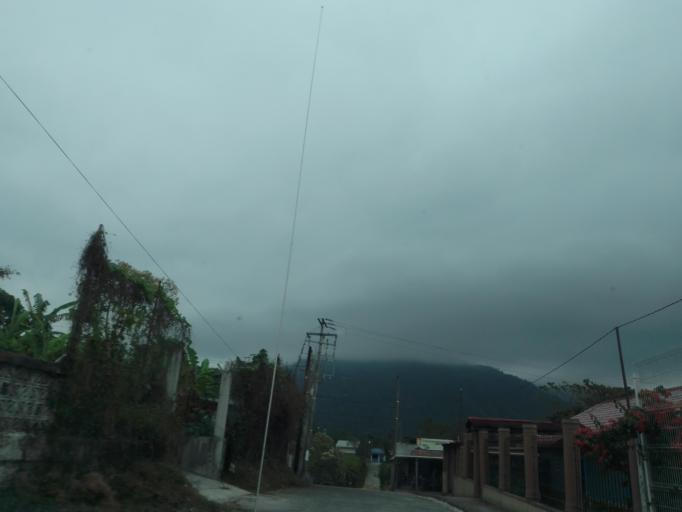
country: MX
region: Chiapas
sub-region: Union Juarez
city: Santo Domingo
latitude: 15.0599
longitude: -92.0804
